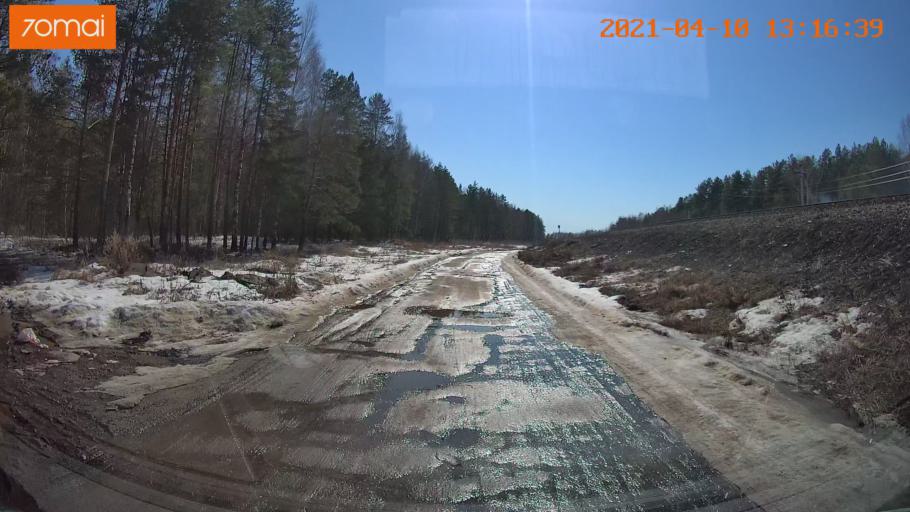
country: RU
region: Ivanovo
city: Bogorodskoye
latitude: 56.9962
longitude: 41.0599
